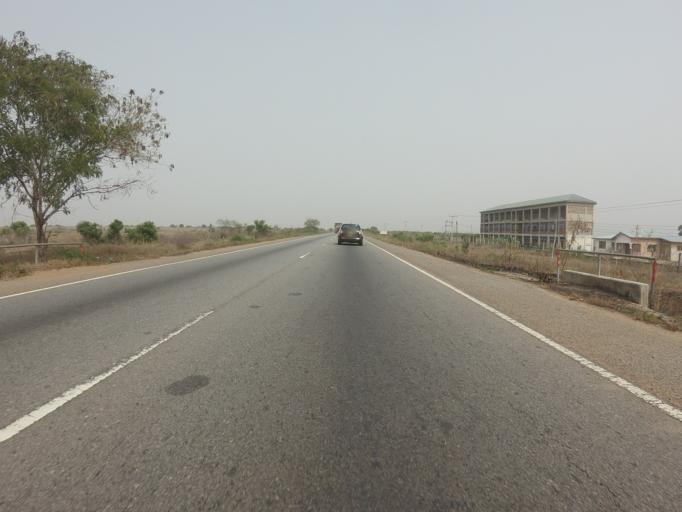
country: GH
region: Greater Accra
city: Tema
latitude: 5.8577
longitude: 0.2706
